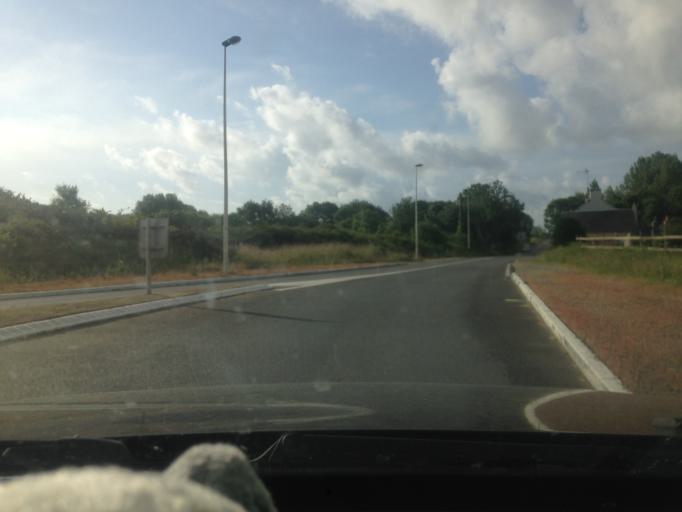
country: FR
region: Brittany
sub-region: Departement du Morbihan
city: Erdeven
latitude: 47.6203
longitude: -3.1351
